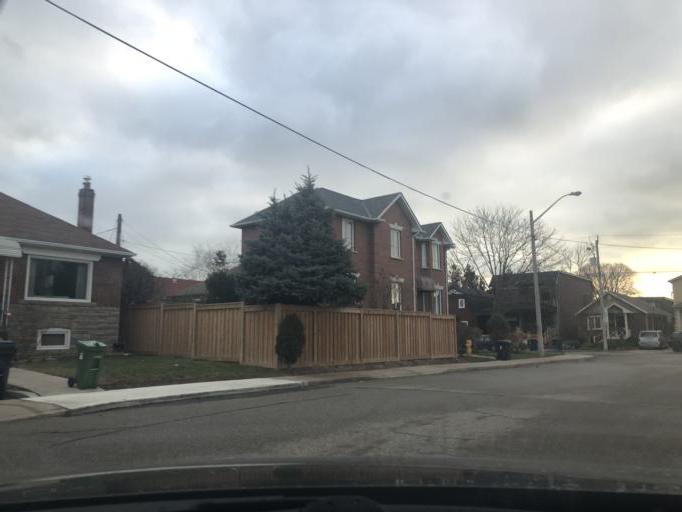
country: CA
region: Ontario
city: Toronto
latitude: 43.6868
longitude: -79.3538
